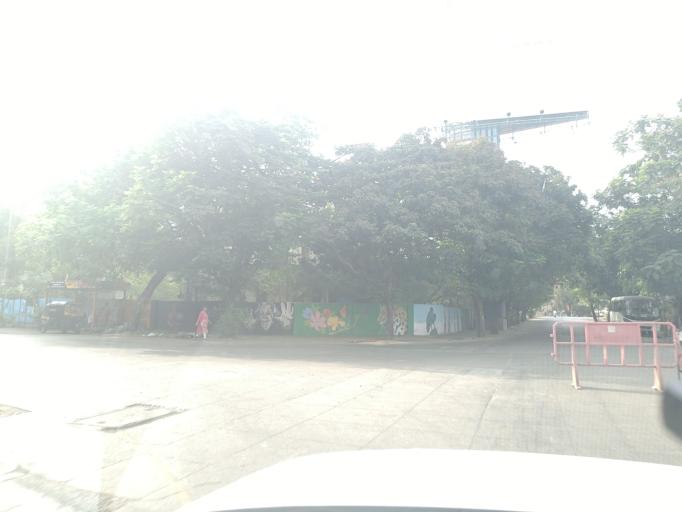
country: IN
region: Maharashtra
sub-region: Thane
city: Thane
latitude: 19.1791
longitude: 72.9677
